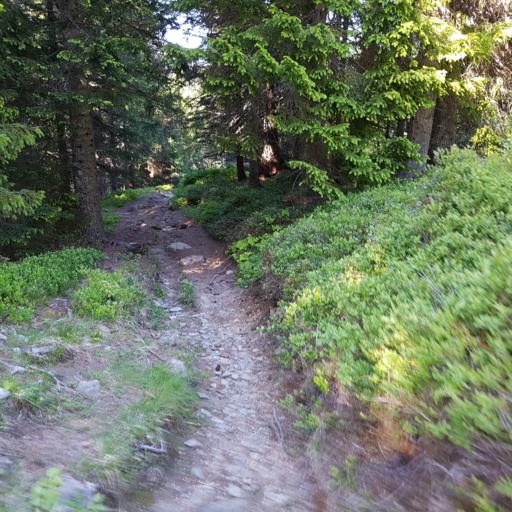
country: NO
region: Sor-Trondelag
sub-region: Trondheim
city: Trondheim
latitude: 63.4147
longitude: 10.3116
